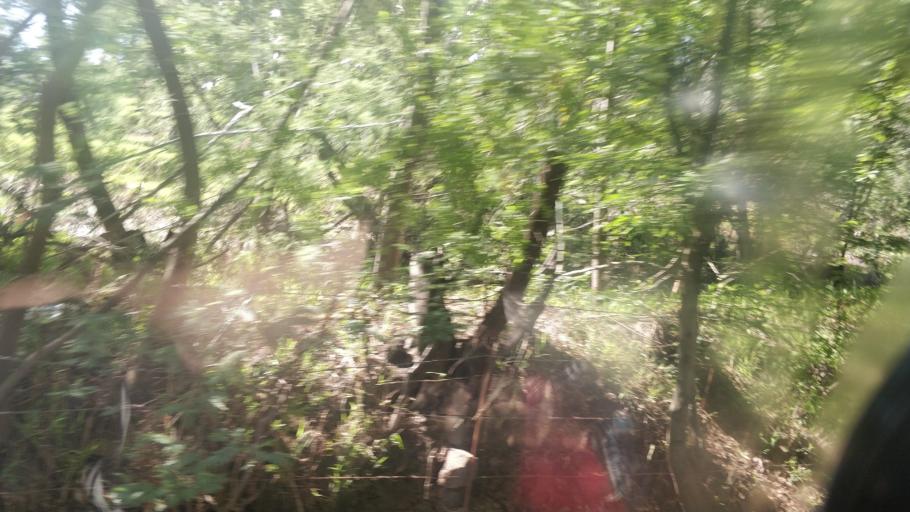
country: LS
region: Maseru
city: Nako
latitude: -29.6268
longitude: 27.5090
